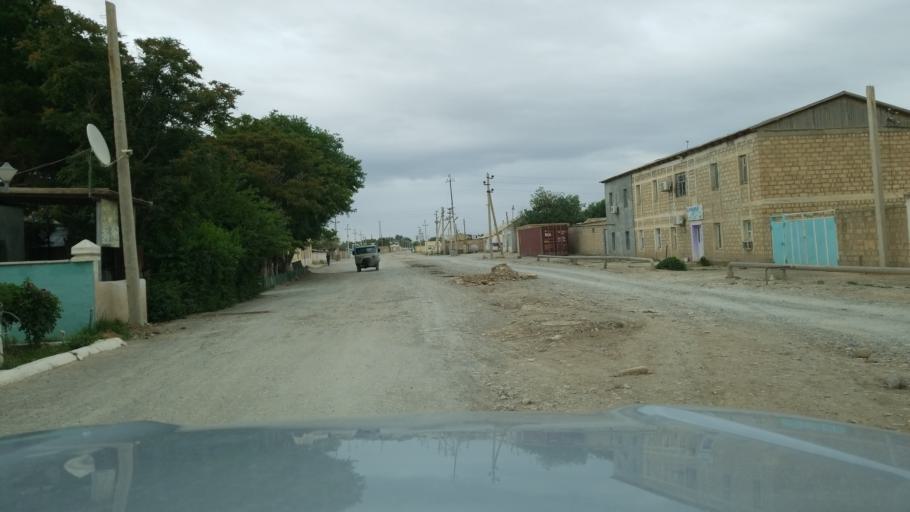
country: TM
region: Balkan
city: Serdar
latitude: 38.9851
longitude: 56.2572
